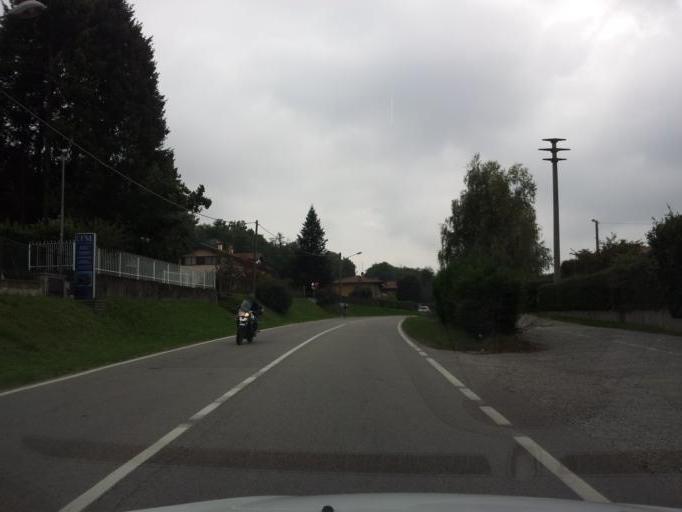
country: IT
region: Lombardy
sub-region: Provincia di Varese
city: Corgeno
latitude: 45.7460
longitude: 8.6909
